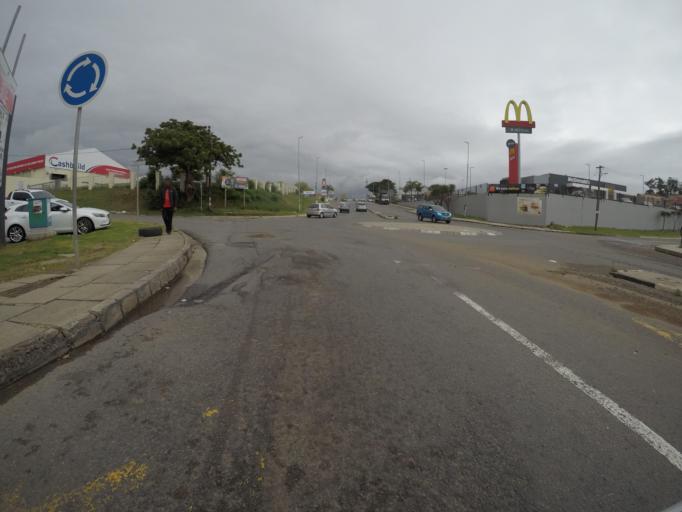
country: ZA
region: Eastern Cape
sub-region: Buffalo City Metropolitan Municipality
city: East London
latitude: -32.9942
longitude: 27.8691
